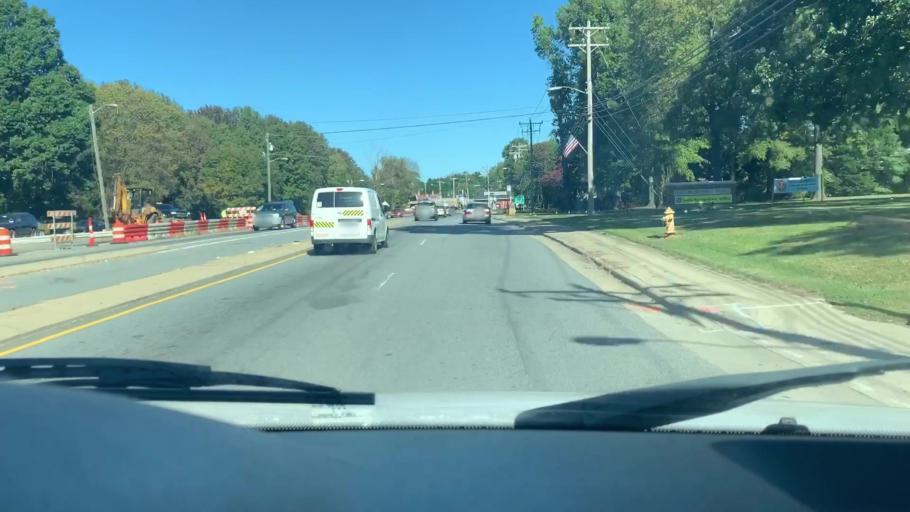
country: US
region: North Carolina
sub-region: Mecklenburg County
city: Charlotte
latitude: 35.2937
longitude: -80.7971
